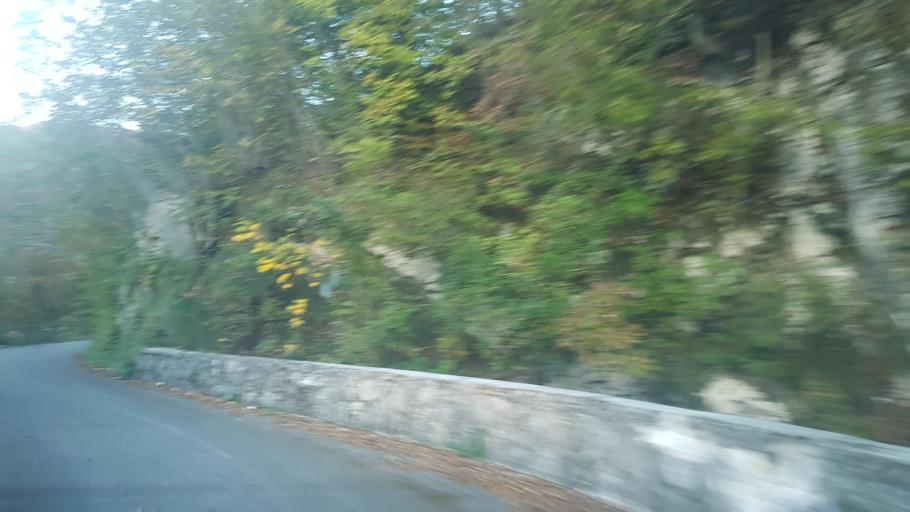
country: IT
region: Friuli Venezia Giulia
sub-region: Provincia di Udine
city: Preone
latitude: 46.3462
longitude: 12.8957
